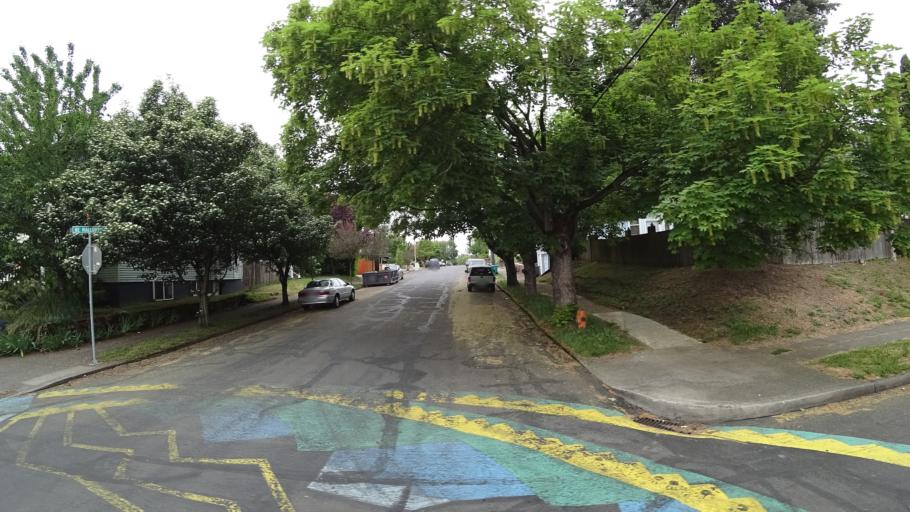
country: US
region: Oregon
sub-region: Multnomah County
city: Portland
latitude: 45.5564
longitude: -122.6635
